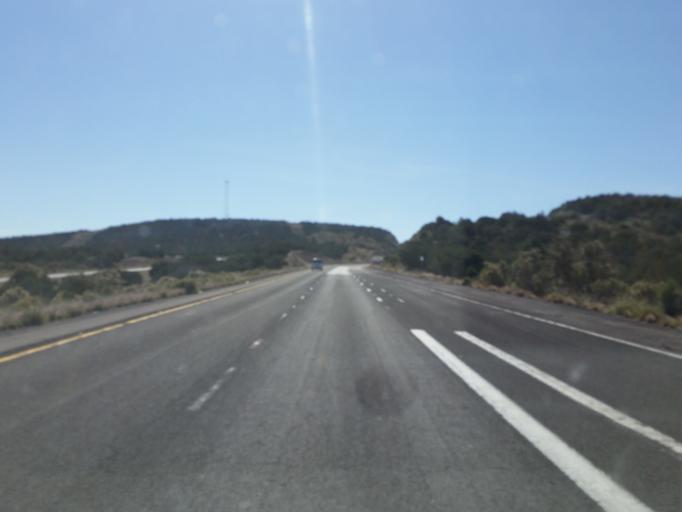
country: US
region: Arizona
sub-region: Mohave County
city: Peach Springs
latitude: 35.1896
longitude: -113.4277
